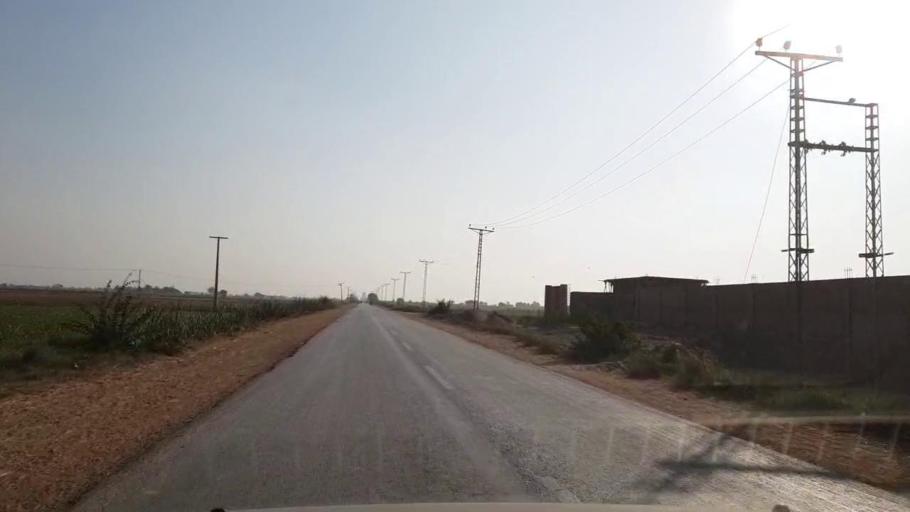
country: PK
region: Sindh
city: Bulri
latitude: 24.8525
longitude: 68.3276
